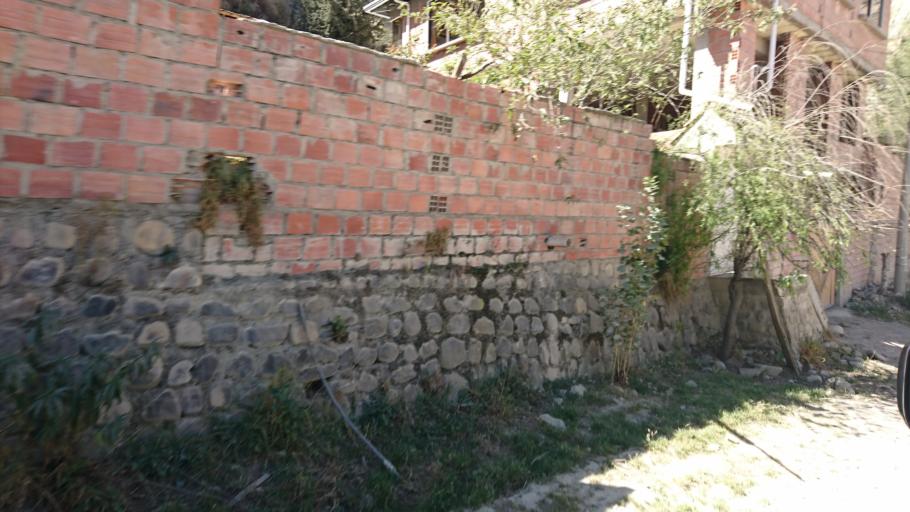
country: BO
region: La Paz
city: La Paz
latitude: -16.4971
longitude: -68.0825
